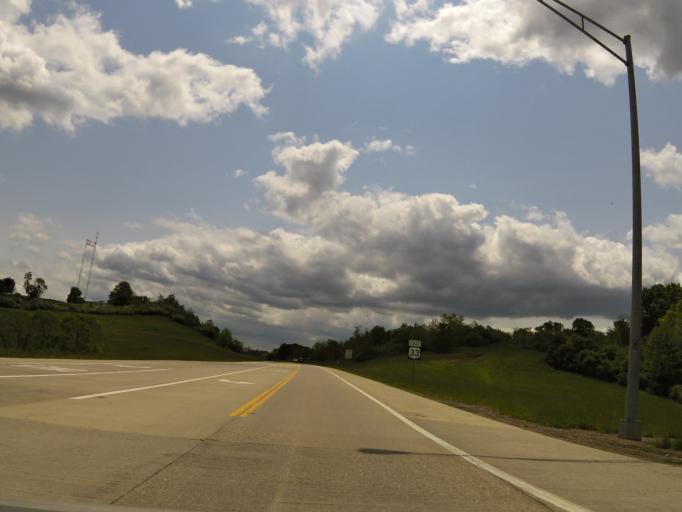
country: US
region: Ohio
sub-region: Athens County
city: Athens
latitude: 39.2385
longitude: -82.0746
